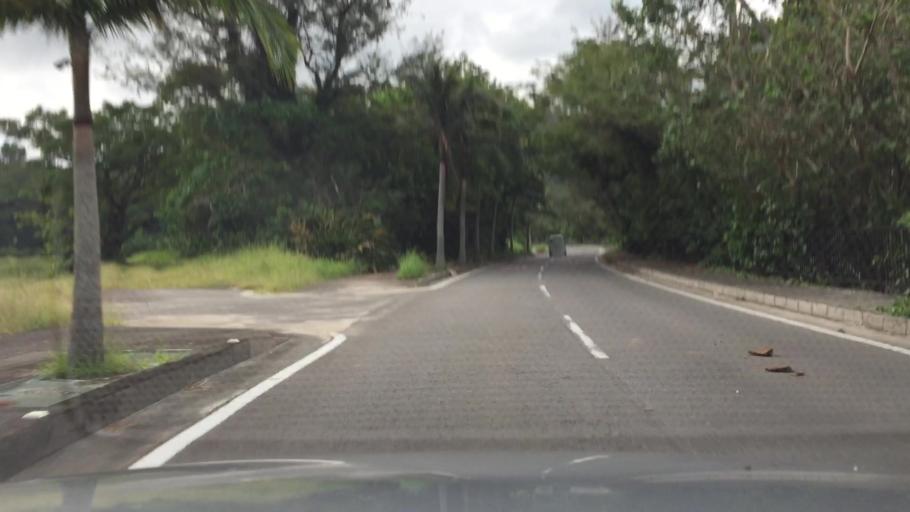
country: JP
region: Okinawa
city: Ishigaki
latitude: 24.4428
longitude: 124.1374
